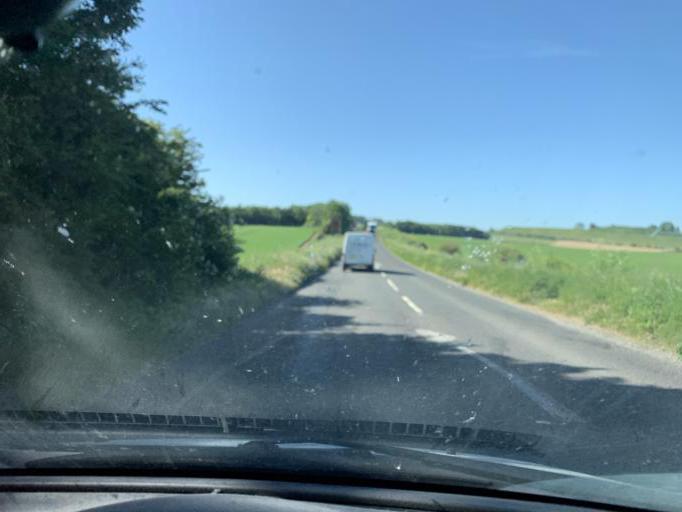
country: GB
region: England
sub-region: Wiltshire
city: Salisbury
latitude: 51.1027
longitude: -1.7960
